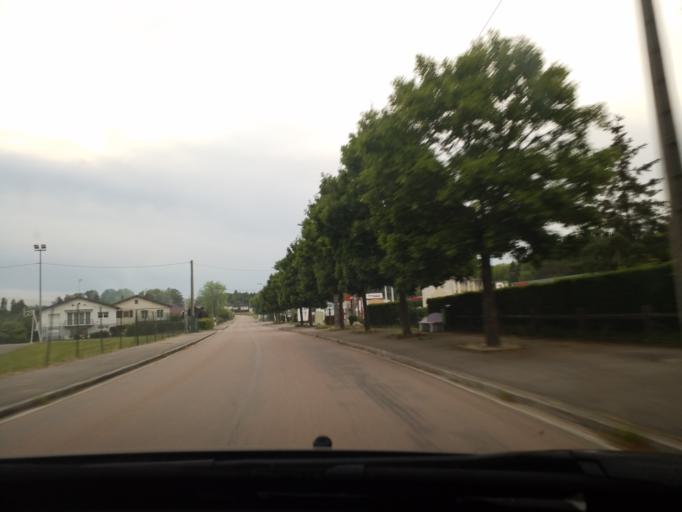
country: FR
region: Lorraine
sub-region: Departement des Vosges
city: Darney
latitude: 48.0931
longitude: 6.0439
